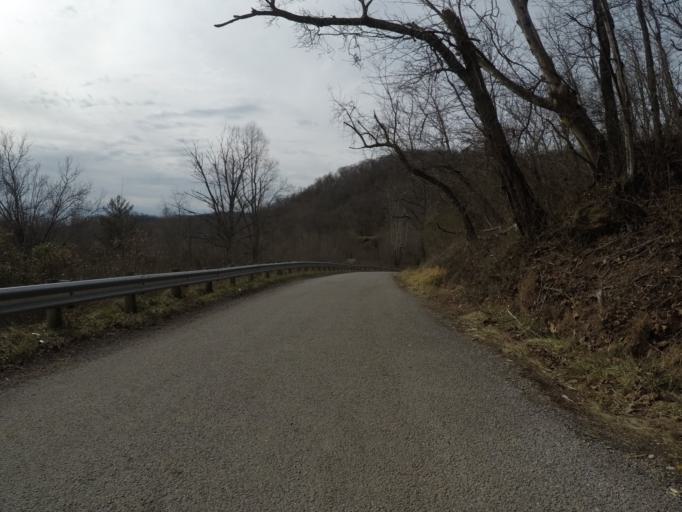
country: US
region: West Virginia
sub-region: Cabell County
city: Huntington
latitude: 38.4416
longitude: -82.4531
